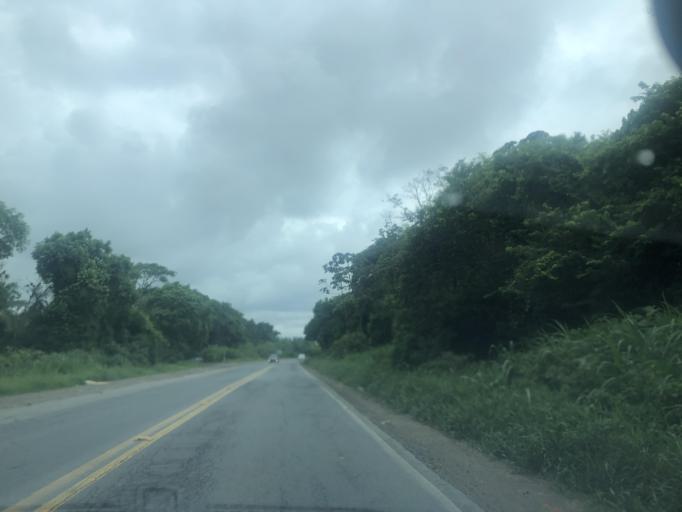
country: BR
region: Santa Catarina
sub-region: Sao Francisco Do Sul
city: Sao Francisco do Sul
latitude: -26.2439
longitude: -48.6162
